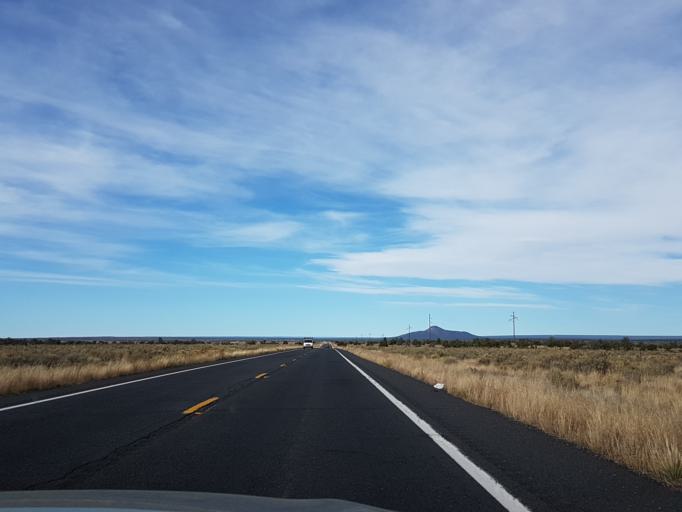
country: US
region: Arizona
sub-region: Coconino County
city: Grand Canyon Village
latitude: 35.6786
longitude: -112.1358
